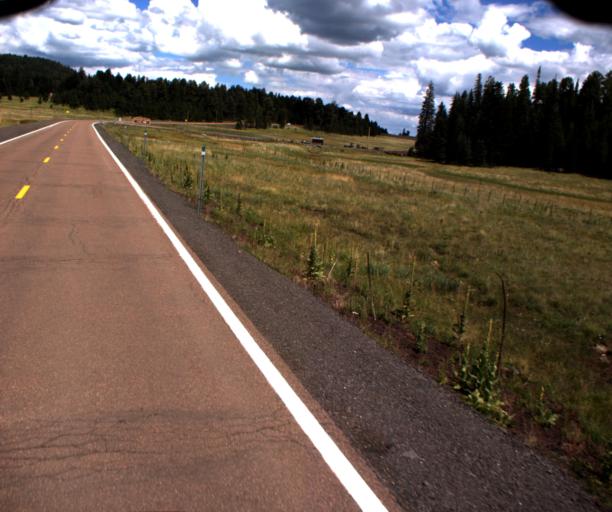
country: US
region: Arizona
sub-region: Apache County
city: Eagar
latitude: 34.0538
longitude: -109.5710
